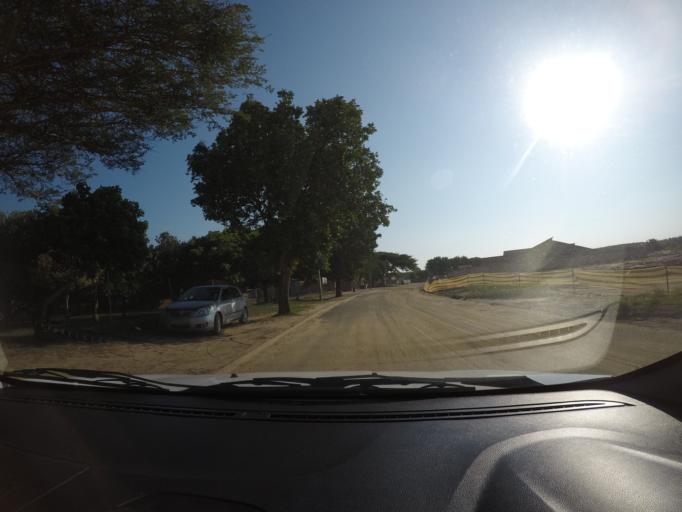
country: ZA
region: KwaZulu-Natal
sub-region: uThungulu District Municipality
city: Richards Bay
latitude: -28.7133
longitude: 32.0343
